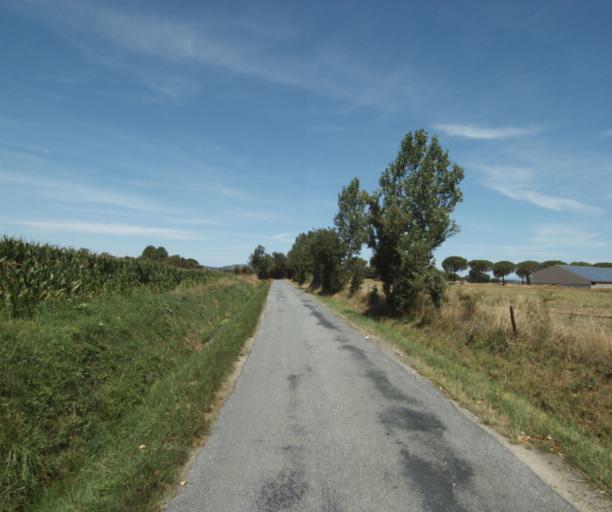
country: FR
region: Midi-Pyrenees
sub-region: Departement de la Haute-Garonne
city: Revel
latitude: 43.5045
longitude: 2.0291
